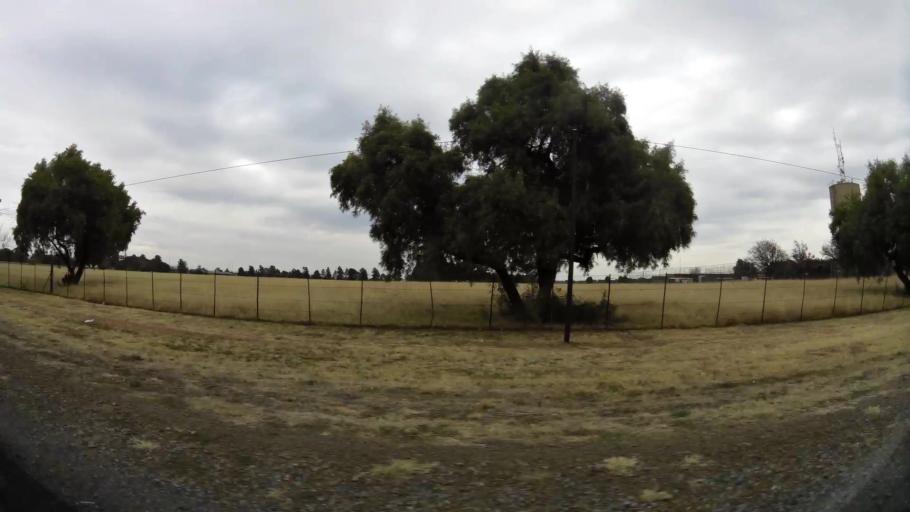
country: ZA
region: Orange Free State
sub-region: Fezile Dabi District Municipality
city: Kroonstad
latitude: -27.6251
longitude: 27.2329
